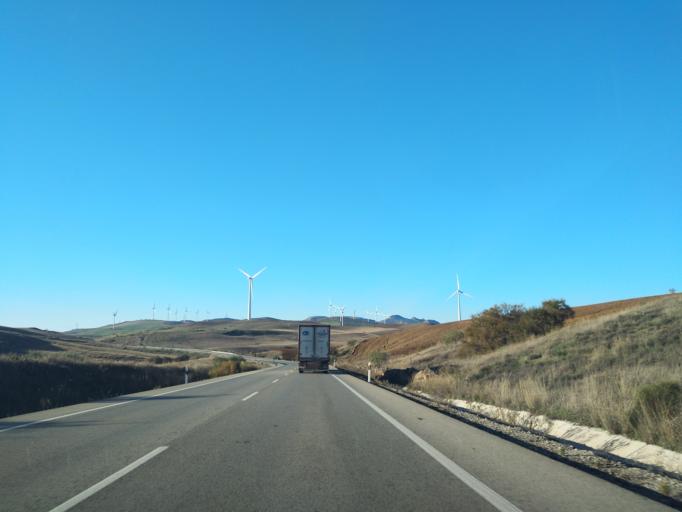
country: ES
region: Andalusia
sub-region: Provincia de Malaga
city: Teba
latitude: 36.9510
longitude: -4.8632
